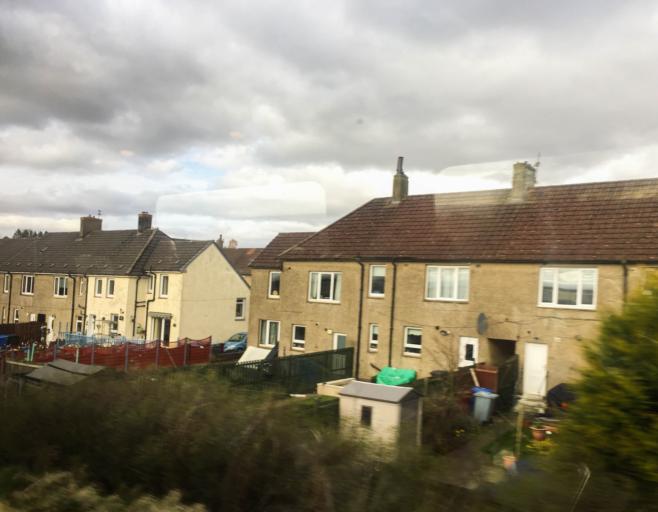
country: GB
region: Scotland
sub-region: South Lanarkshire
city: Carluke
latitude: 55.7288
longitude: -3.8454
